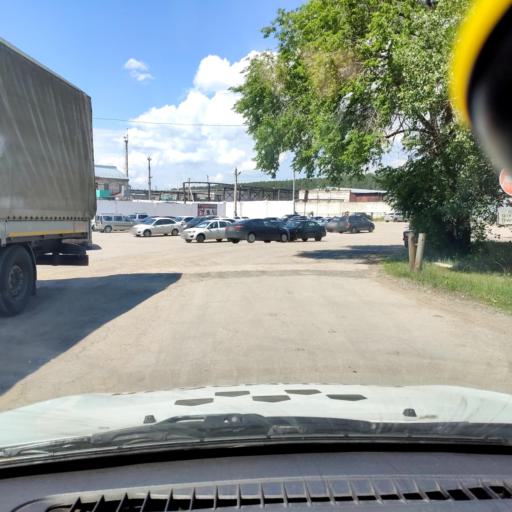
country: RU
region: Samara
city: Zhigulevsk
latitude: 53.4702
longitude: 49.5615
